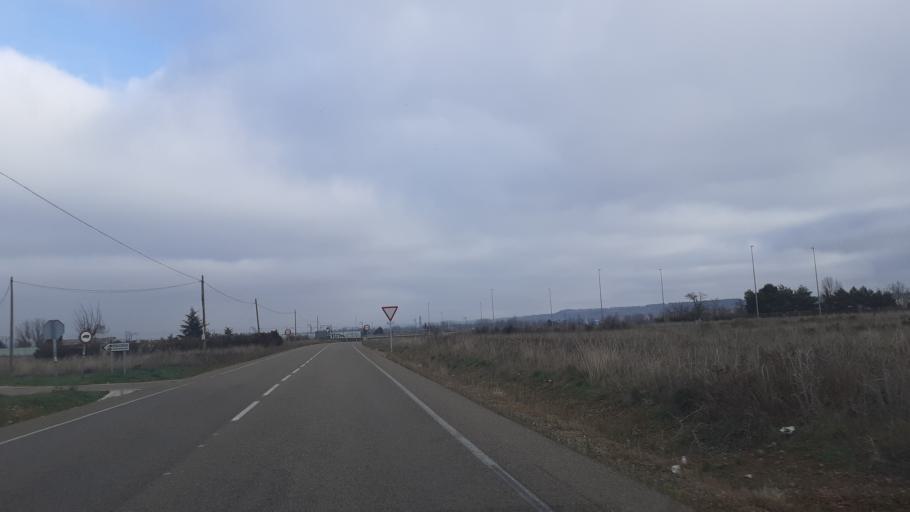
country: ES
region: Castille and Leon
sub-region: Provincia de Leon
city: Onzonilla
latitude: 42.5542
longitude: -5.5842
